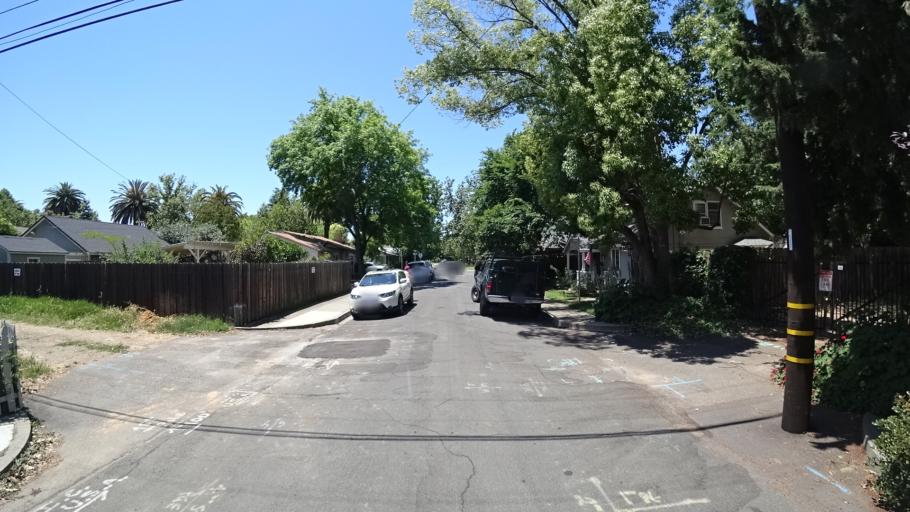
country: US
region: California
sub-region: Sacramento County
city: Parkway
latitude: 38.5343
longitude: -121.4426
